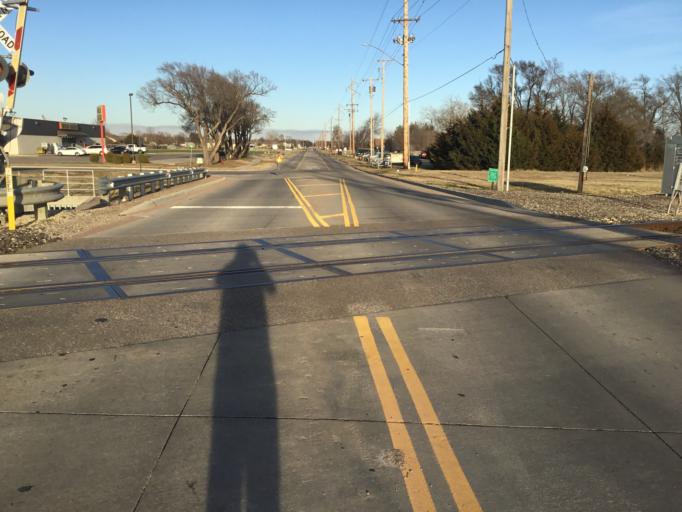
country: US
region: Kansas
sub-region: Sedgwick County
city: Valley Center
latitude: 37.8250
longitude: -97.3712
